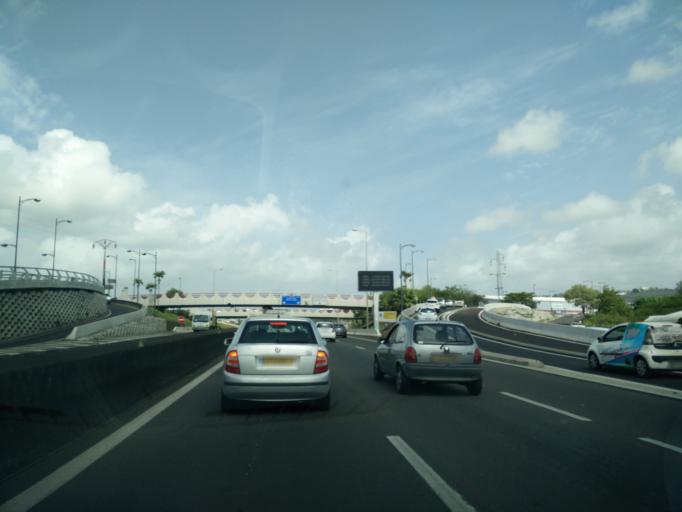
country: MQ
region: Martinique
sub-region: Martinique
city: Le Lamentin
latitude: 14.6181
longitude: -61.0299
